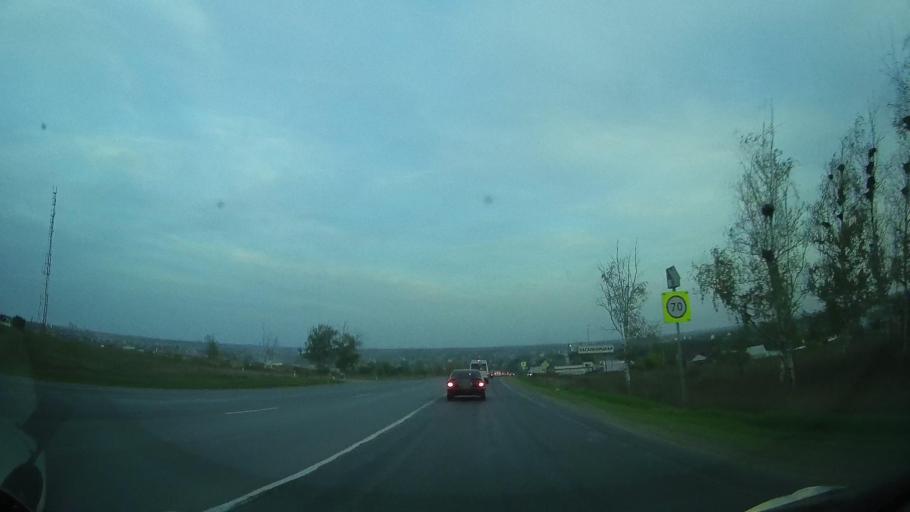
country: RU
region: Rostov
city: Kagal'nitskaya
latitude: 46.8882
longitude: 40.1394
